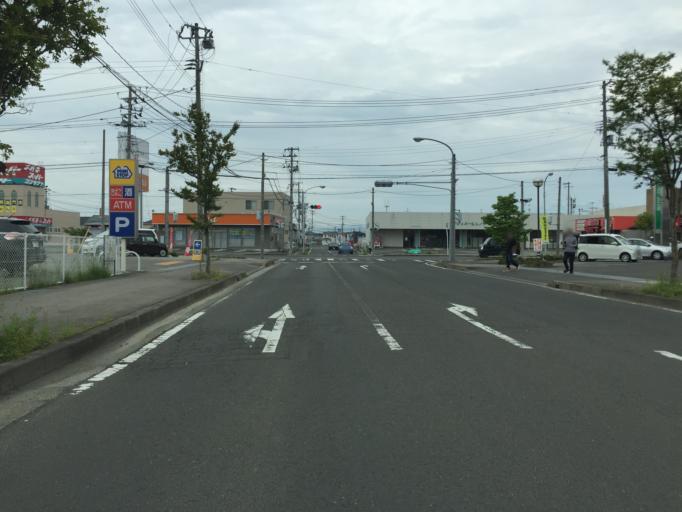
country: JP
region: Fukushima
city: Fukushima-shi
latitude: 37.7889
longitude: 140.4545
